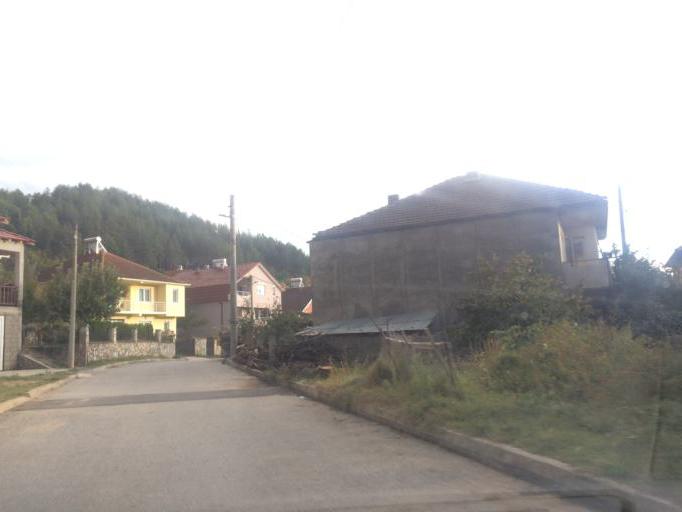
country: MK
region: Makedonska Kamenica
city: Makedonska Kamenica
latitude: 42.0180
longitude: 22.5921
